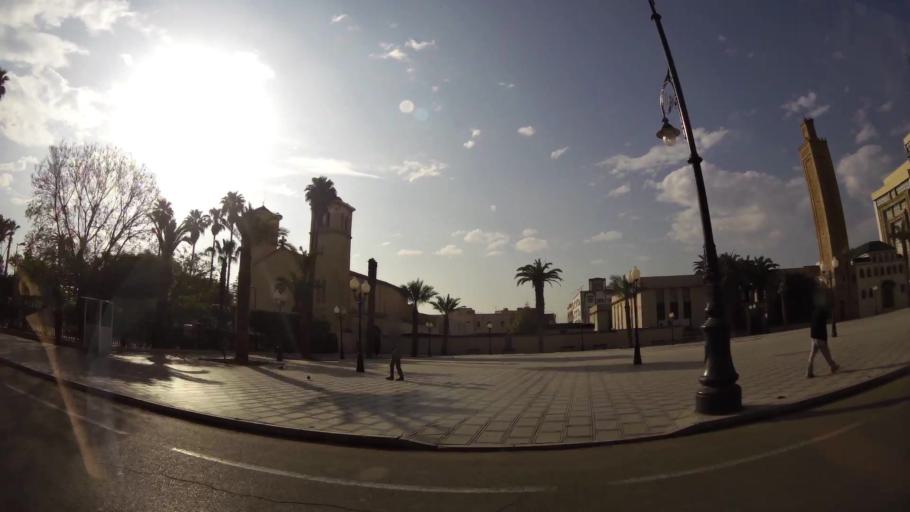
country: MA
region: Oriental
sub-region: Oujda-Angad
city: Oujda
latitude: 34.6798
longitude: -1.9182
